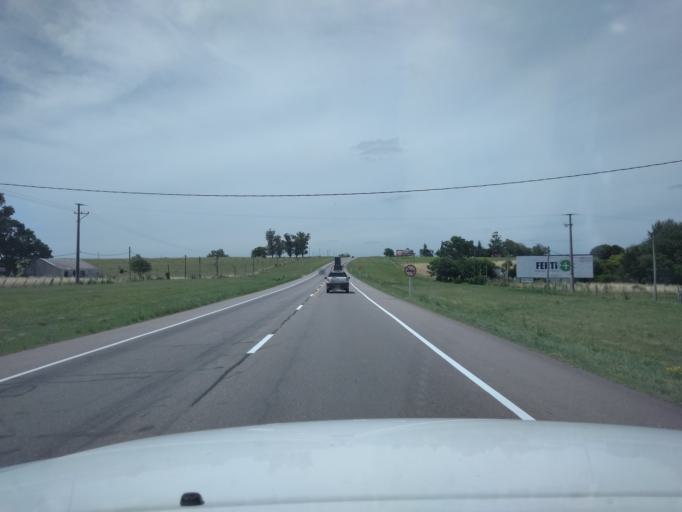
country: UY
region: Florida
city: Florida
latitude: -34.1728
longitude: -56.1885
